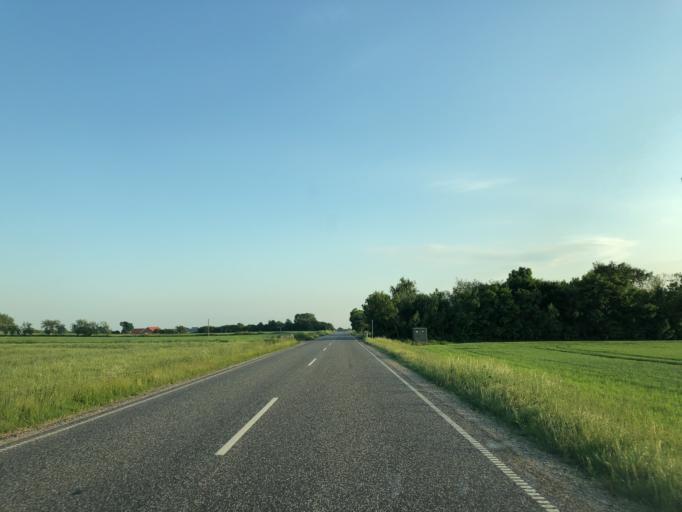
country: DK
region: Central Jutland
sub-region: Struer Kommune
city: Struer
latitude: 56.4501
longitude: 8.5370
